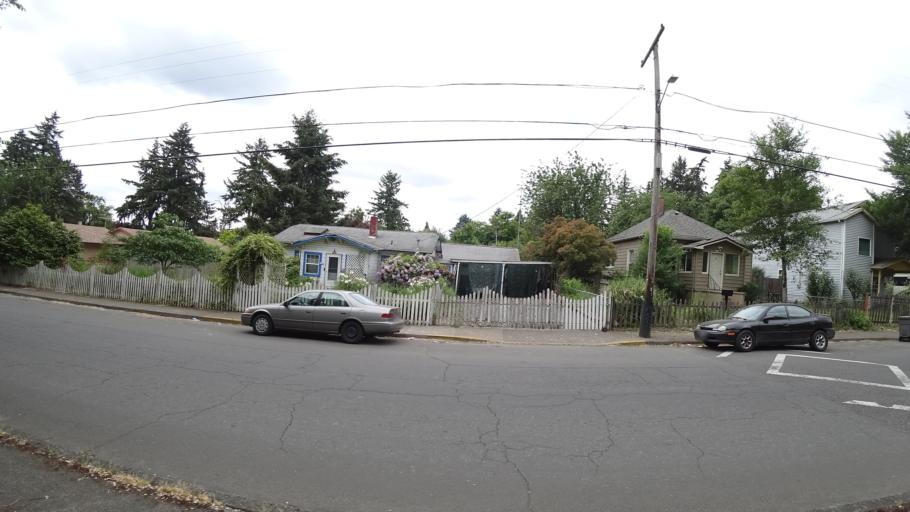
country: US
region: Oregon
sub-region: Multnomah County
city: Lents
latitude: 45.4855
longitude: -122.5722
